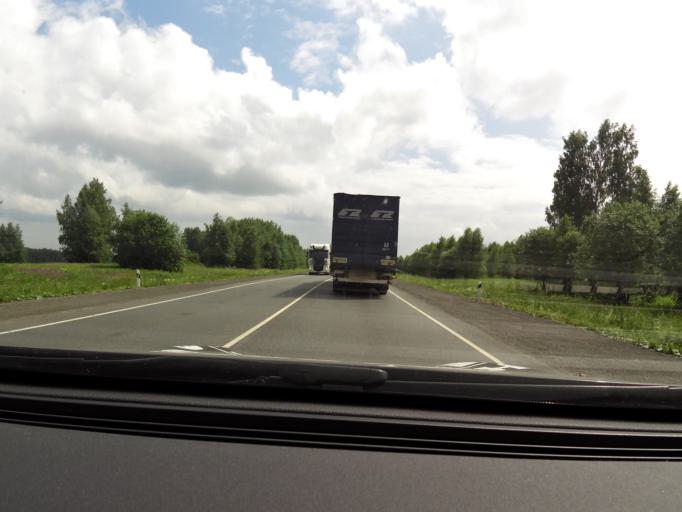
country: RU
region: Perm
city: Ust'-Kishert'
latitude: 57.1670
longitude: 57.1505
